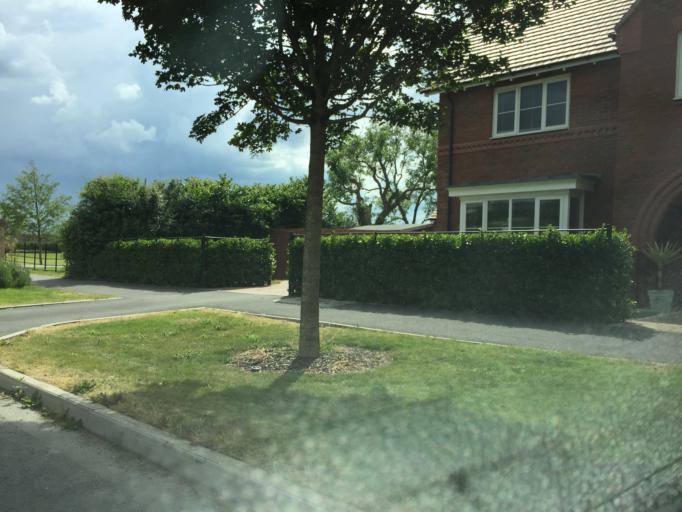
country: GB
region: England
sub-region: Borough of Swindon
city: Broad Blunsdon
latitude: 51.6078
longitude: -1.8155
